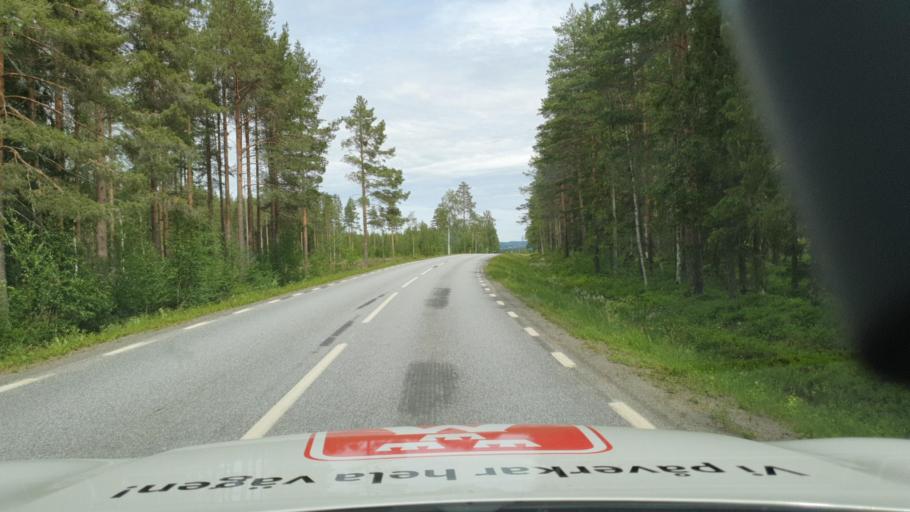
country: SE
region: Vaesterbotten
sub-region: Skelleftea Kommun
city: Burtraesk
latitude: 64.4059
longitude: 20.3874
